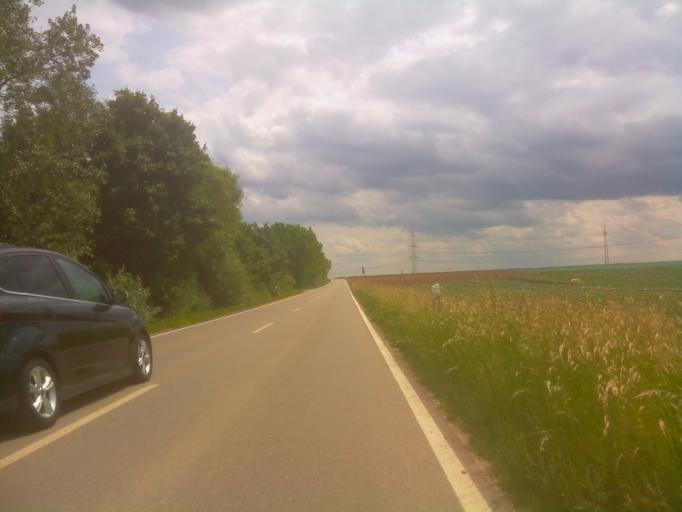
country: DE
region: Rheinland-Pfalz
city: Gerolsheim
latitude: 49.5348
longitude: 8.2796
